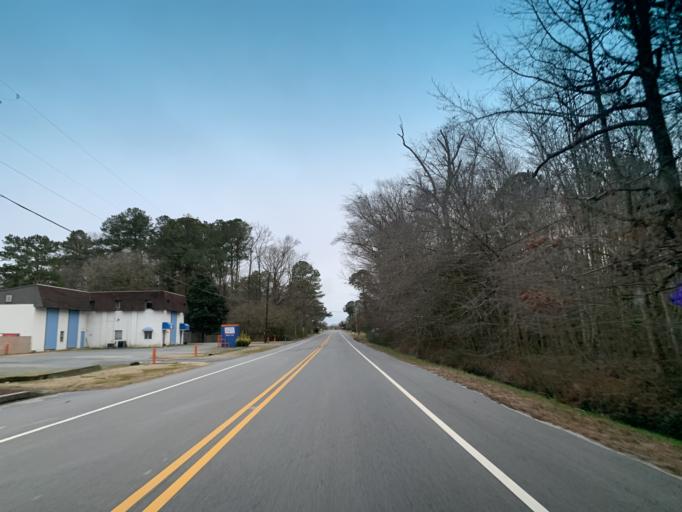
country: US
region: Maryland
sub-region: Worcester County
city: Pocomoke City
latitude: 38.0724
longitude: -75.5463
